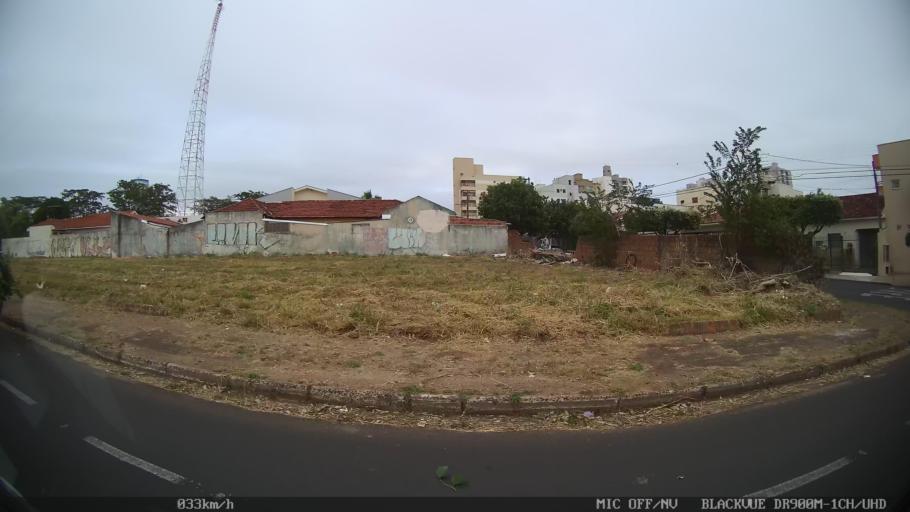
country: BR
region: Sao Paulo
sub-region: Sao Jose Do Rio Preto
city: Sao Jose do Rio Preto
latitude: -20.8394
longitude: -49.3844
